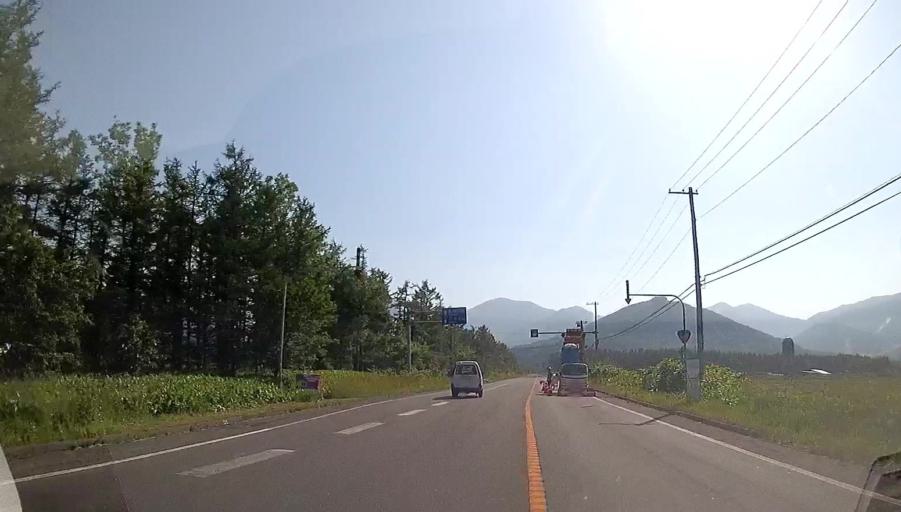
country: JP
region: Hokkaido
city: Otofuke
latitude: 42.9765
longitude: 142.8235
